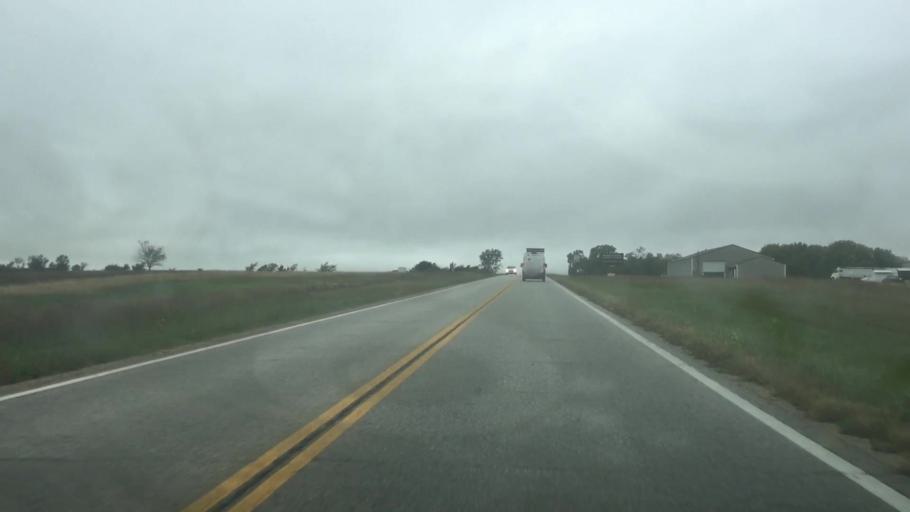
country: US
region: Kansas
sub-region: Anderson County
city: Garnett
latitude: 38.1680
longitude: -95.2899
